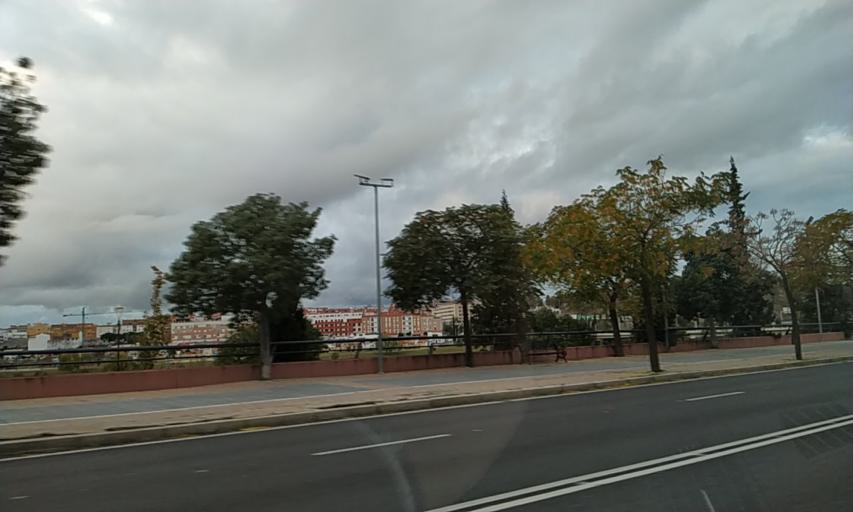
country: ES
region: Extremadura
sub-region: Provincia de Badajoz
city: Badajoz
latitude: 38.8817
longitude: -6.9746
